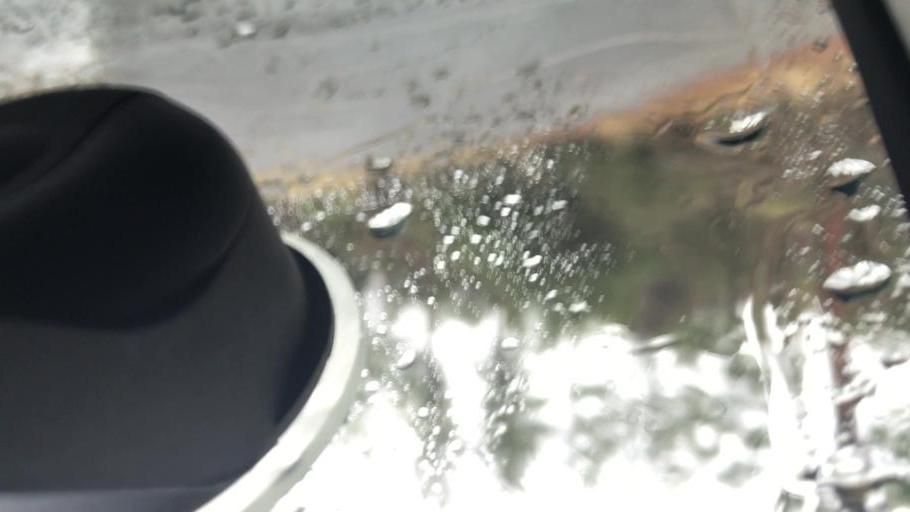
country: US
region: Arizona
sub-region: Yavapai County
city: Prescott
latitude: 34.5070
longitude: -112.3838
